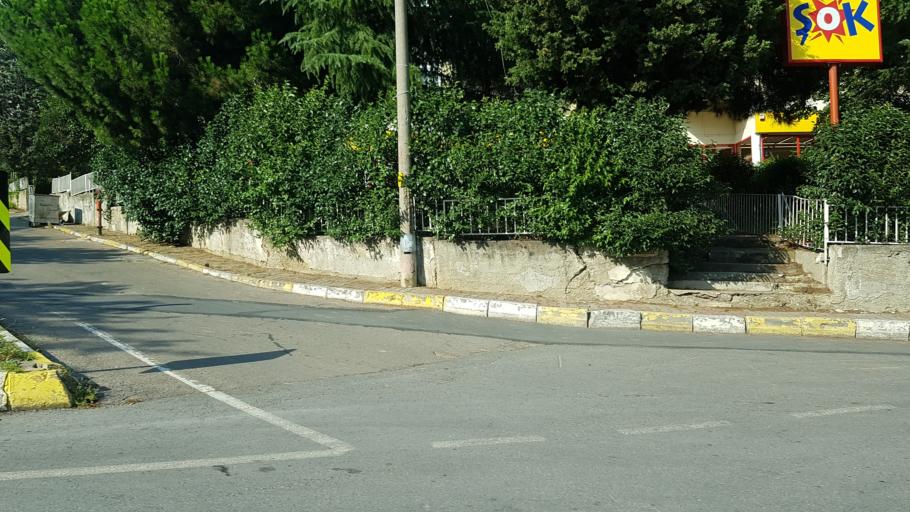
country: TR
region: Istanbul
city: Maltepe
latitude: 40.9231
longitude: 29.1602
